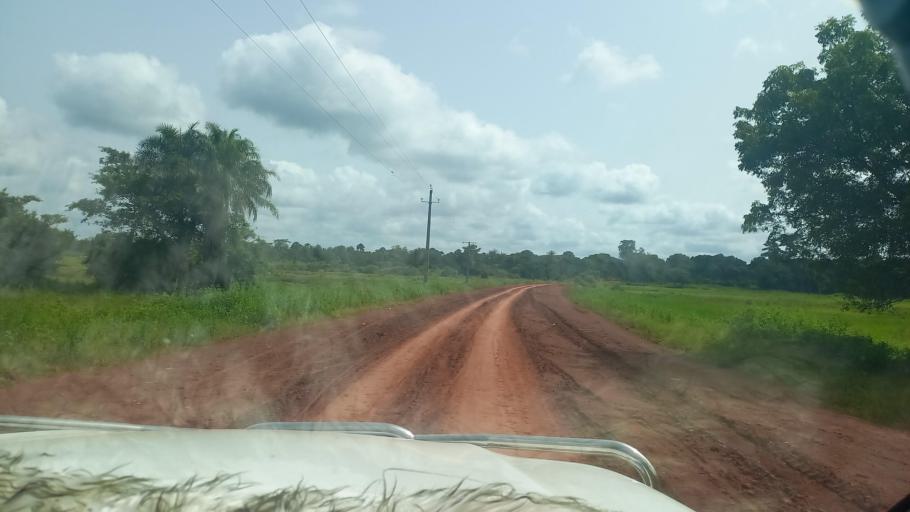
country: SN
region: Ziguinchor
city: Bignona
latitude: 12.7543
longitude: -16.2748
